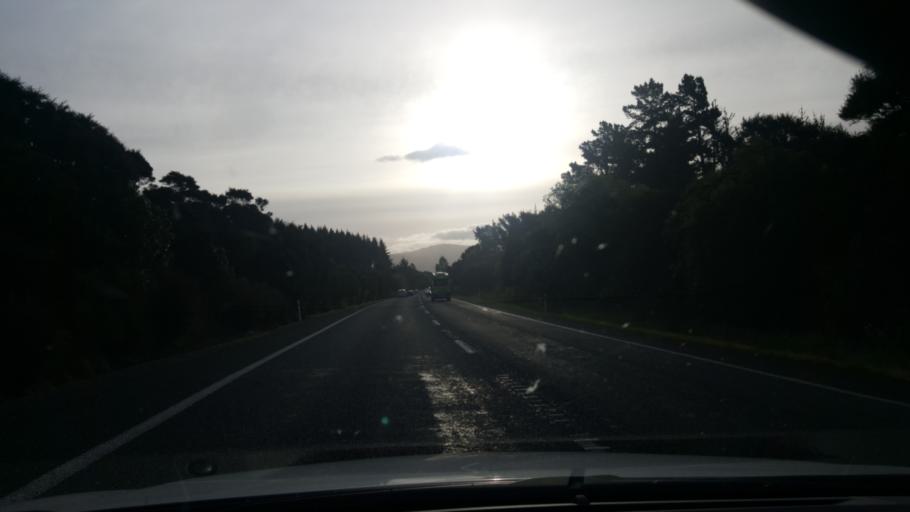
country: NZ
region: Waikato
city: Turangi
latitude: -38.9362
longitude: 175.8676
